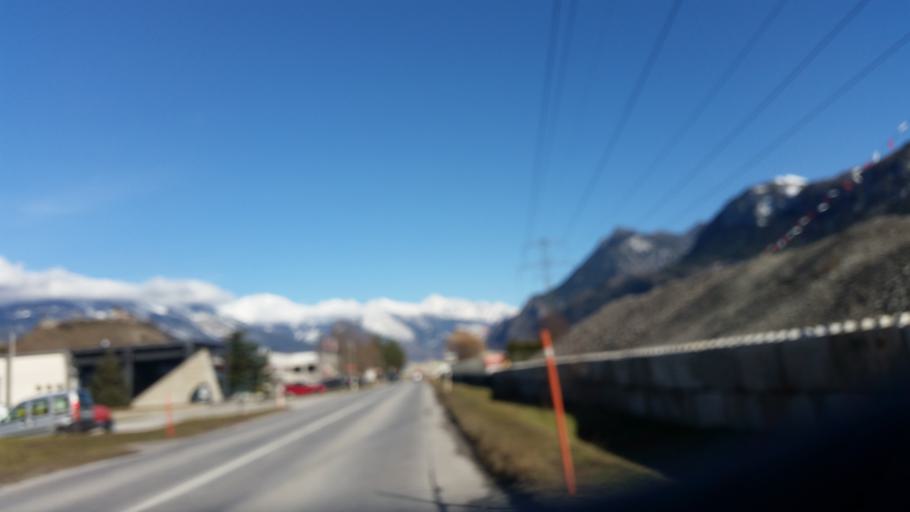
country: CH
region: Valais
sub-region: Sierre District
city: Grone
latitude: 46.2586
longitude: 7.4733
